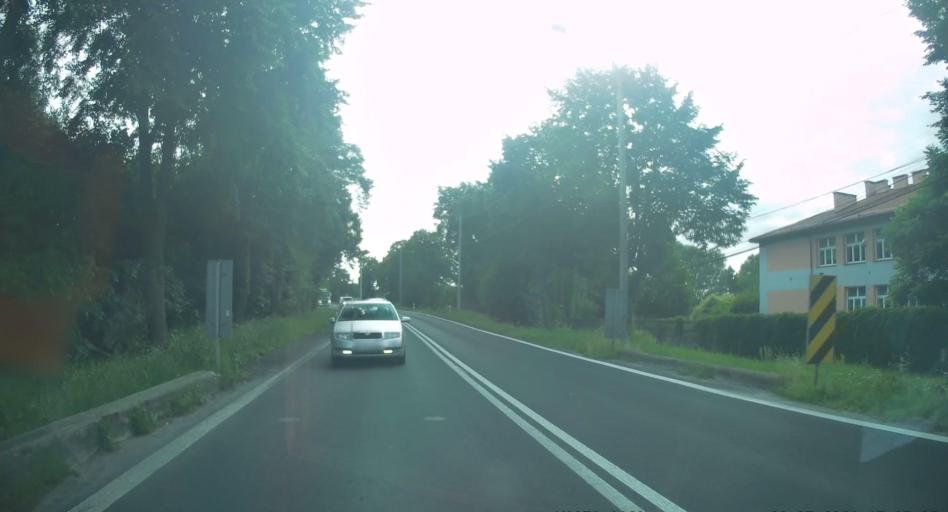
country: PL
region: Silesian Voivodeship
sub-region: Powiat czestochowski
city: Borowno
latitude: 50.9120
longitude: 19.3081
